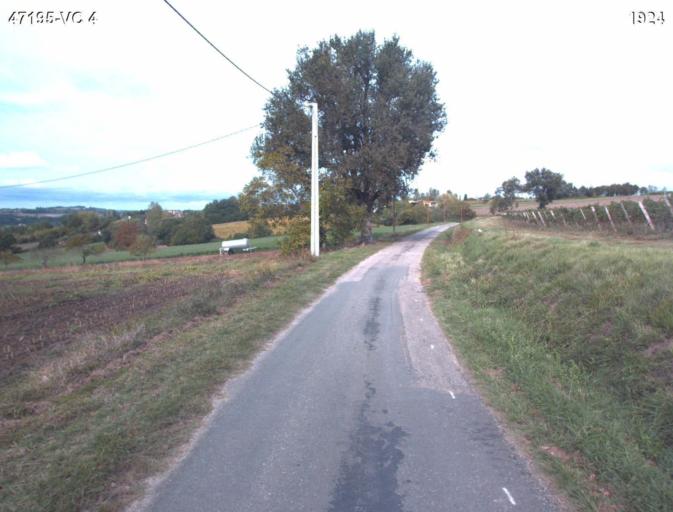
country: FR
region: Aquitaine
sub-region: Departement du Lot-et-Garonne
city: Nerac
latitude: 44.1063
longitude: 0.3873
